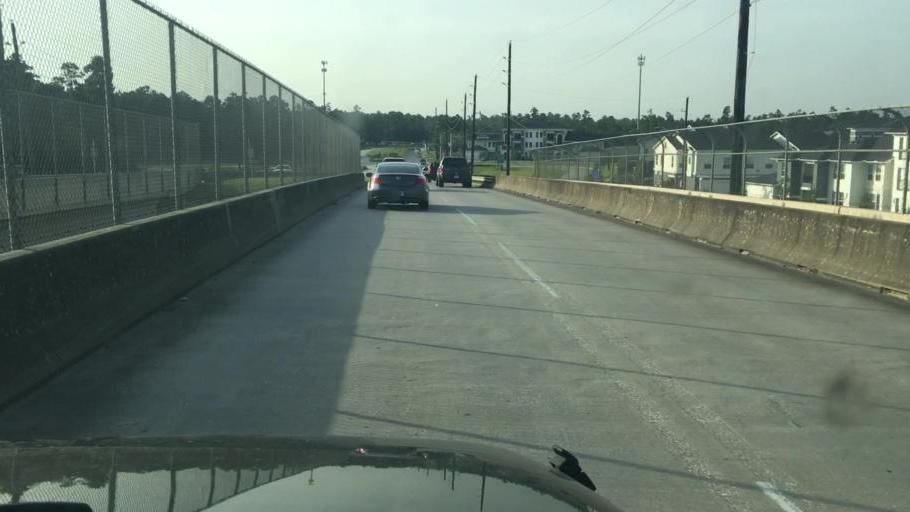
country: US
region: Texas
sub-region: Harris County
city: Atascocita
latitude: 29.9681
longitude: -95.1701
